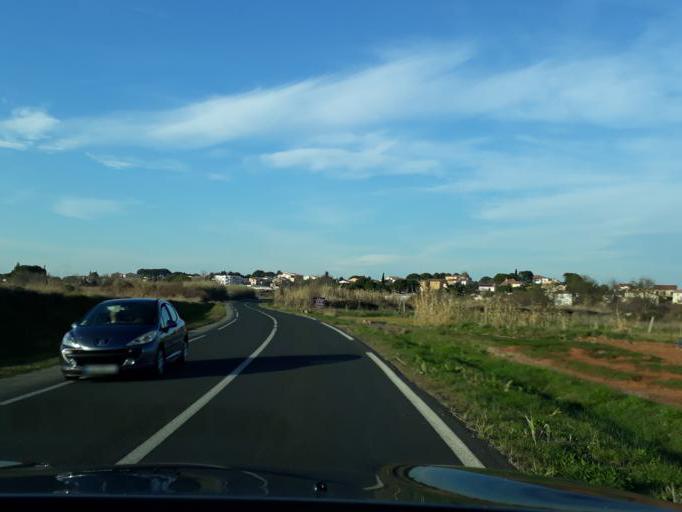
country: FR
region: Languedoc-Roussillon
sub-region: Departement de l'Herault
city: Marseillan
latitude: 43.3451
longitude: 3.5259
